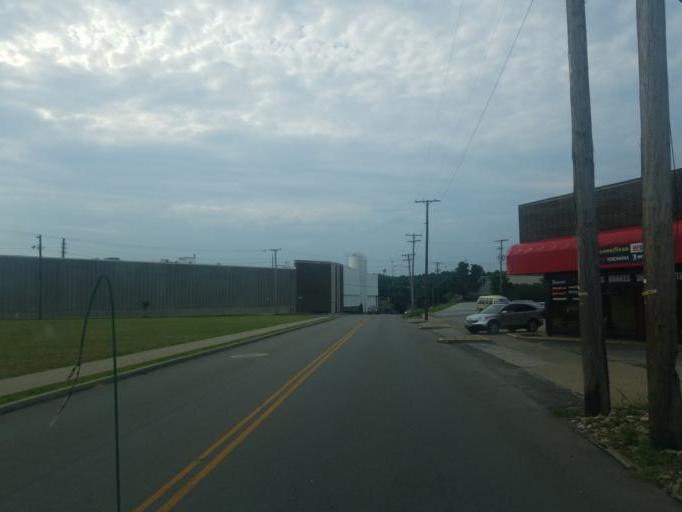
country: US
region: Ohio
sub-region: Wayne County
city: Wooster
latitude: 40.7937
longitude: -81.9385
